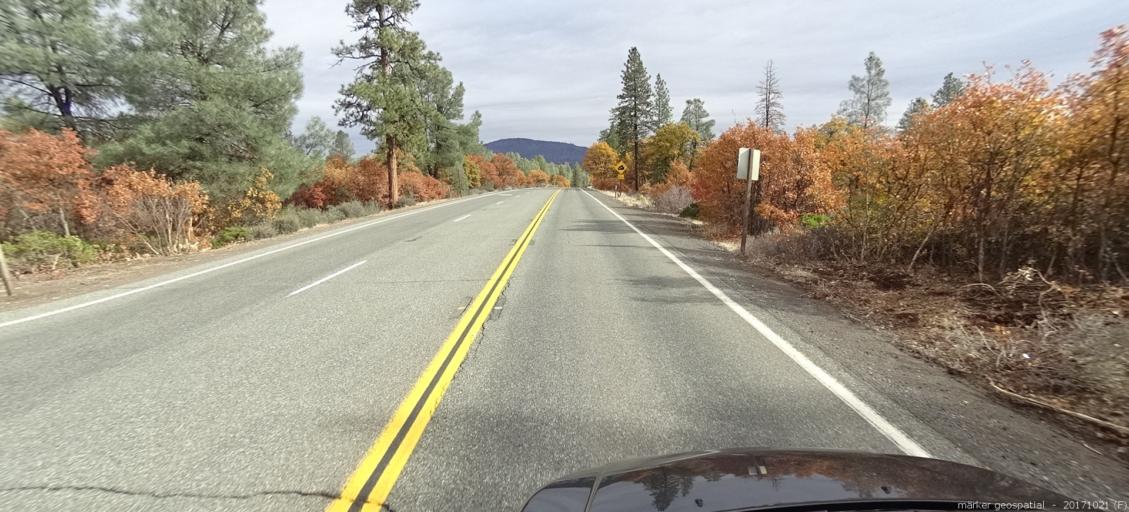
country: US
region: California
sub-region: Shasta County
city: Burney
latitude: 40.9665
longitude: -121.5737
